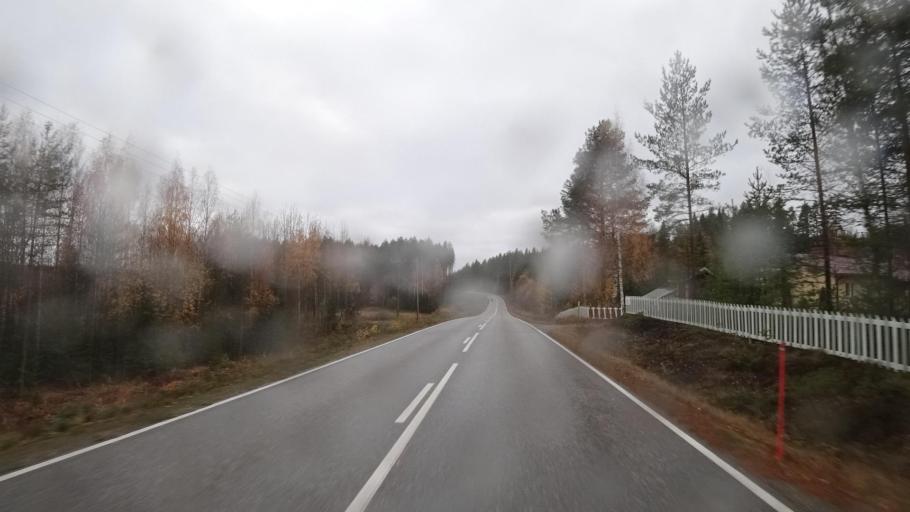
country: FI
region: North Karelia
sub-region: Joensuu
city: Outokumpu
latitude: 62.6201
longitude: 28.9284
